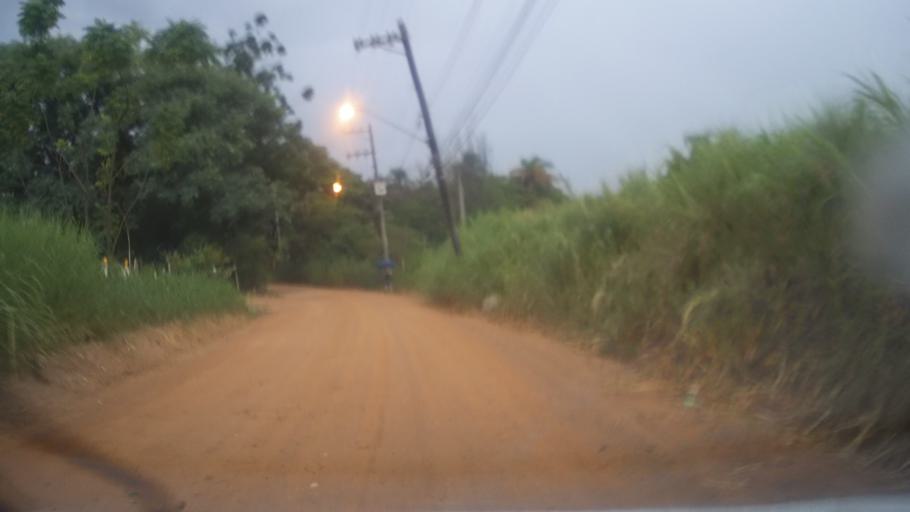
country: BR
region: Sao Paulo
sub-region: Itupeva
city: Itupeva
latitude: -23.1930
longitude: -46.9941
